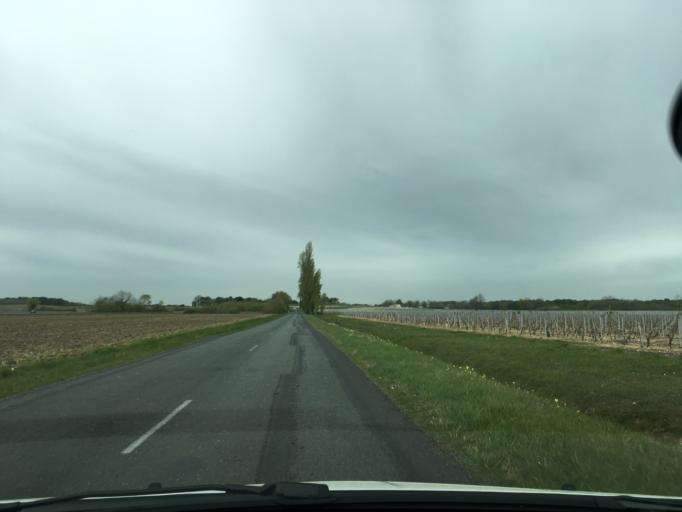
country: FR
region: Aquitaine
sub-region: Departement de la Gironde
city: Lesparre-Medoc
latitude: 45.3241
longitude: -0.8913
